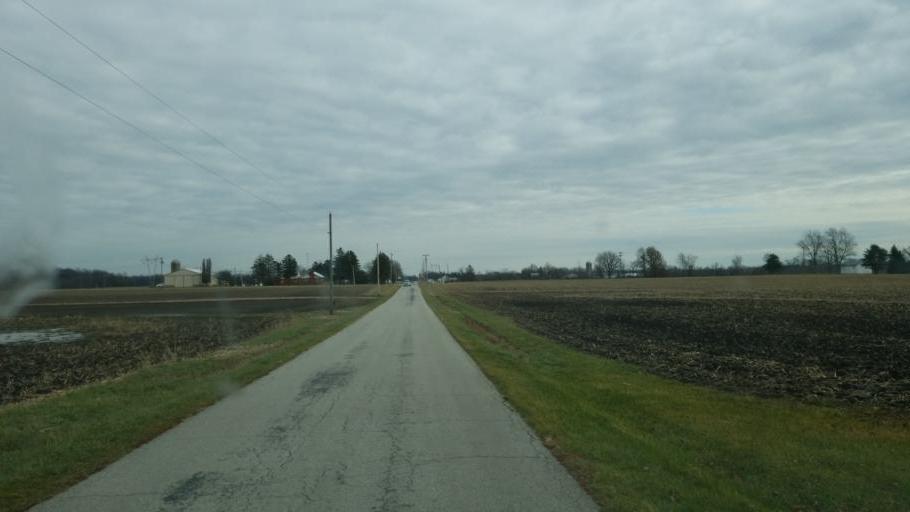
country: US
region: Ohio
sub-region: Crawford County
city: Bucyrus
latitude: 40.7399
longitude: -82.9399
